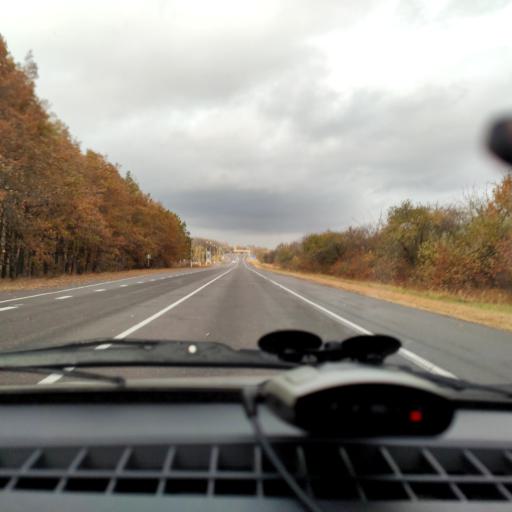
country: RU
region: Voronezj
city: Kolodeznyy
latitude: 51.3308
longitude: 39.0261
